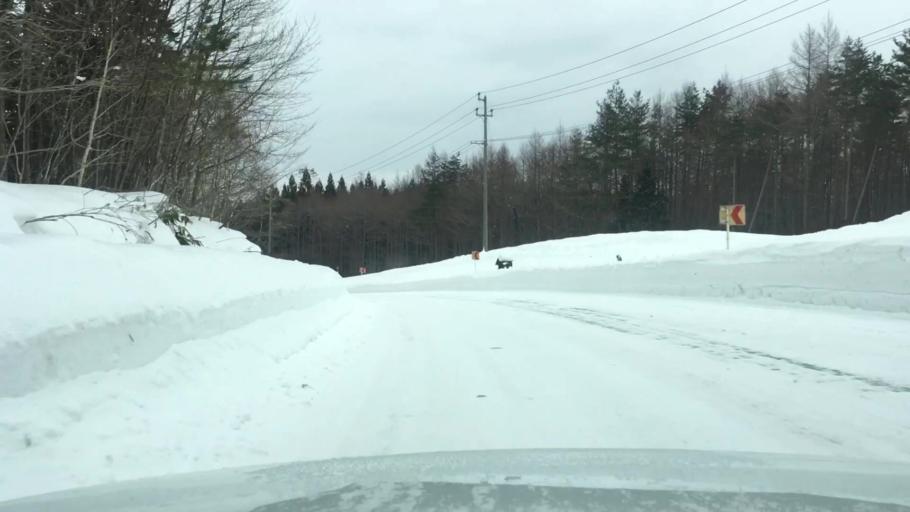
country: JP
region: Iwate
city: Shizukuishi
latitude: 39.9835
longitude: 141.0037
